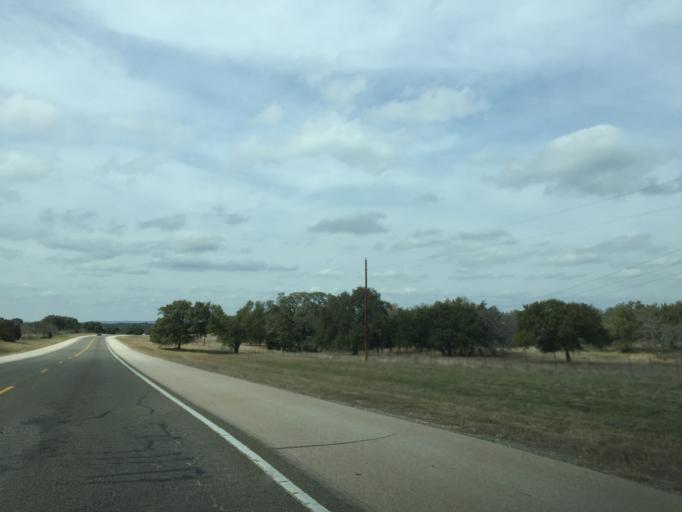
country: US
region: Texas
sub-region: Burnet County
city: Granite Shoals
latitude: 30.5316
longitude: -98.4336
